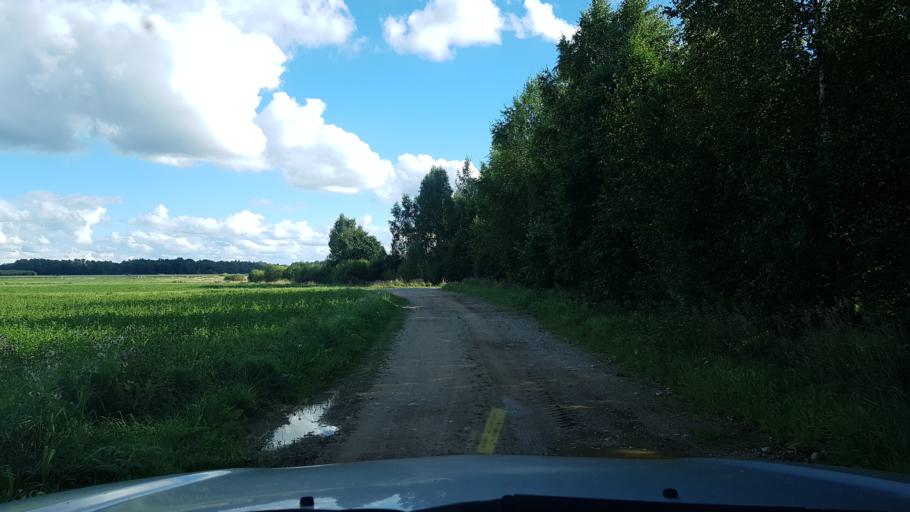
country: EE
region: Harju
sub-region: Rae vald
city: Jueri
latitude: 59.3527
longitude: 24.8577
